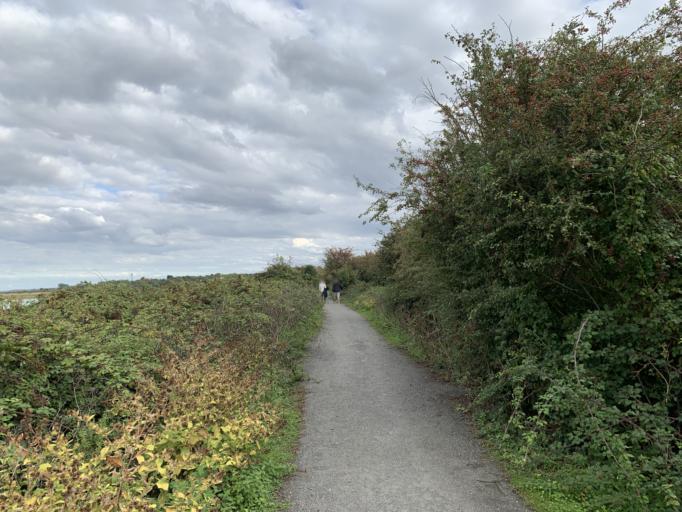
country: GB
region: England
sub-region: Kent
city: Cliffe
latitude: 51.4644
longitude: 0.4707
